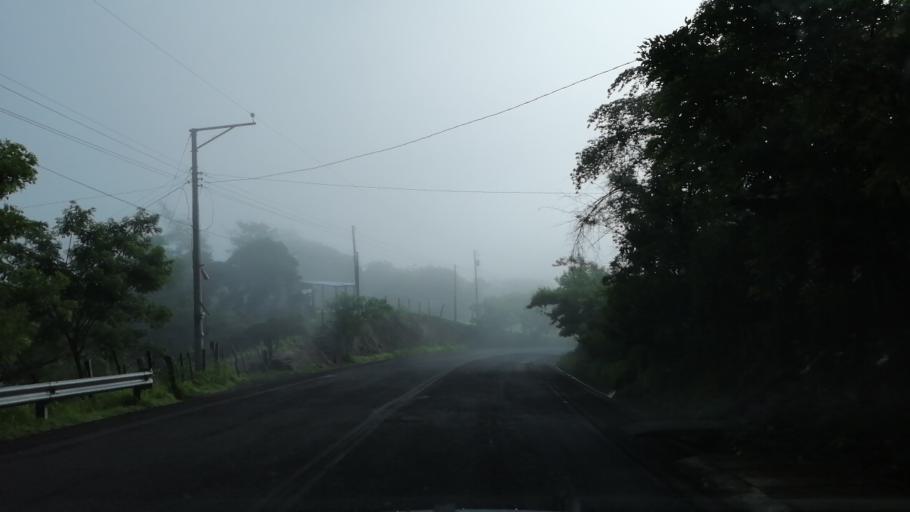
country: SV
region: Morazan
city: Cacaopera
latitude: 13.7880
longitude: -88.1159
